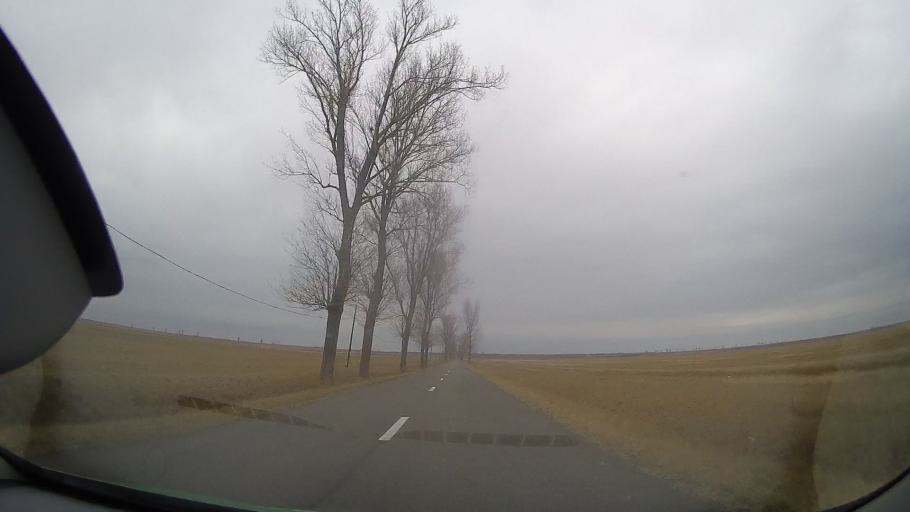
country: RO
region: Braila
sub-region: Comuna Rosiori
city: Rosiori
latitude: 44.8227
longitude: 27.4000
